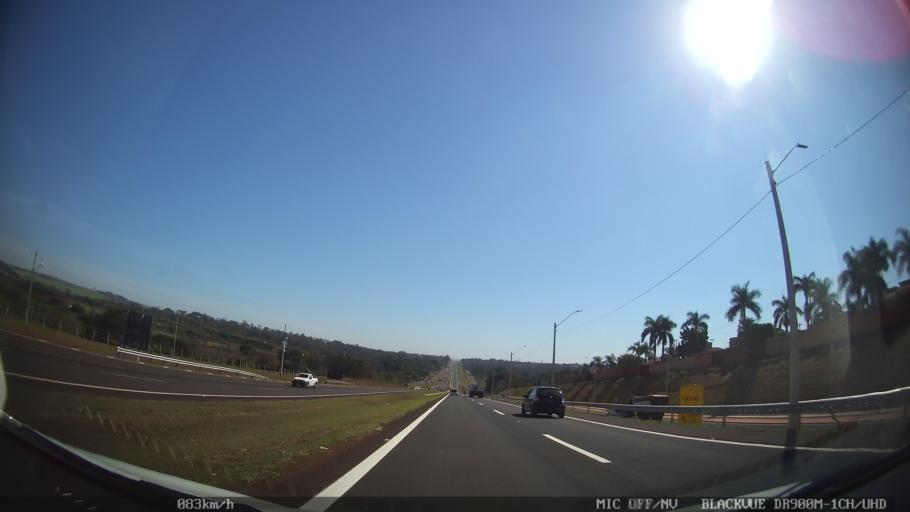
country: BR
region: Sao Paulo
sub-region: Ribeirao Preto
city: Ribeirao Preto
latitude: -21.2181
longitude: -47.8309
